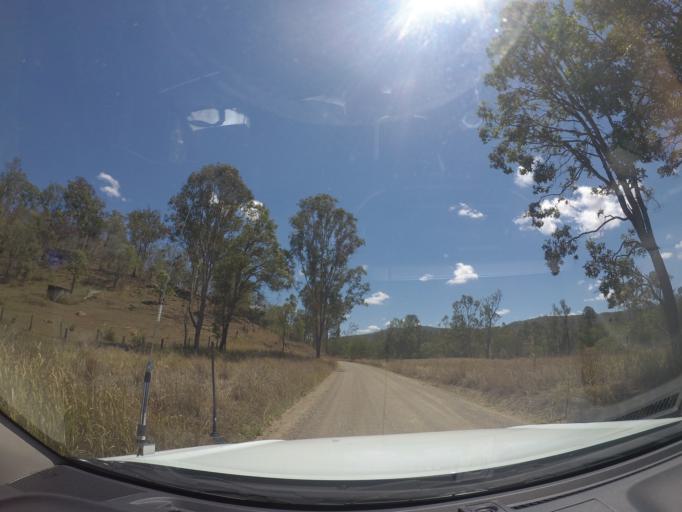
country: AU
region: Queensland
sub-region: Ipswich
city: Springfield Lakes
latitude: -27.8199
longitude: 152.8577
